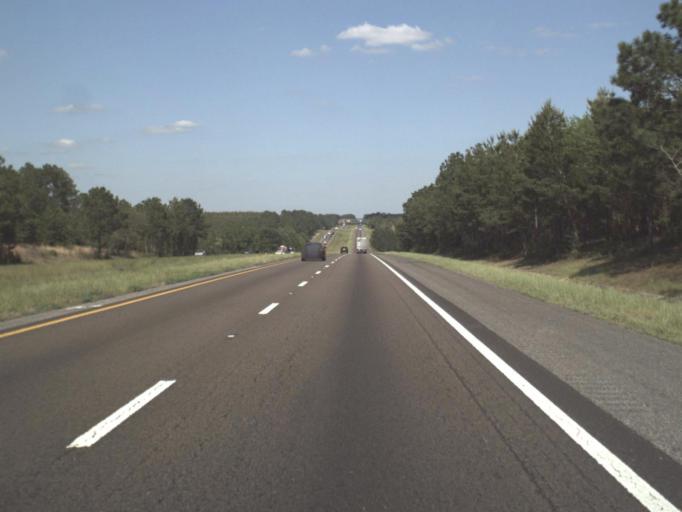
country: US
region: Florida
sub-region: Santa Rosa County
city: East Milton
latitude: 30.6792
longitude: -86.8140
